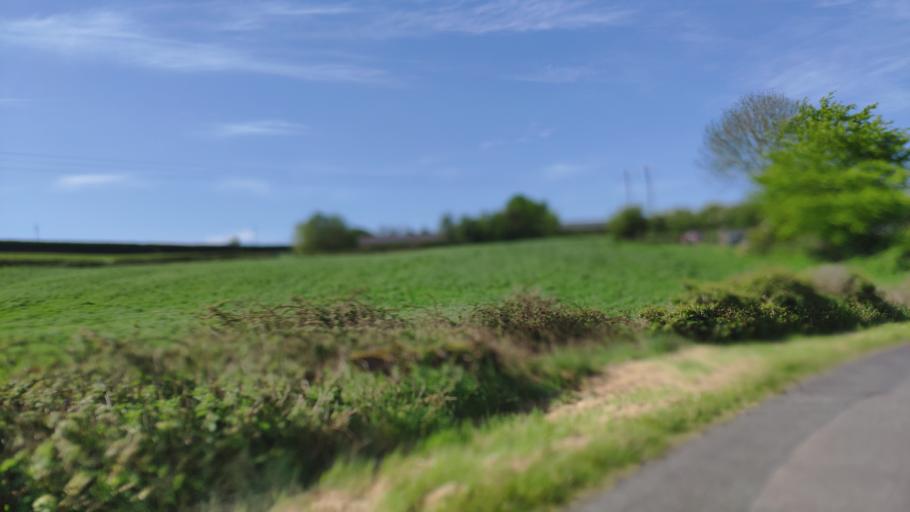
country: IE
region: Munster
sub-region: County Cork
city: Blarney
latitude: 51.9177
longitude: -8.5363
